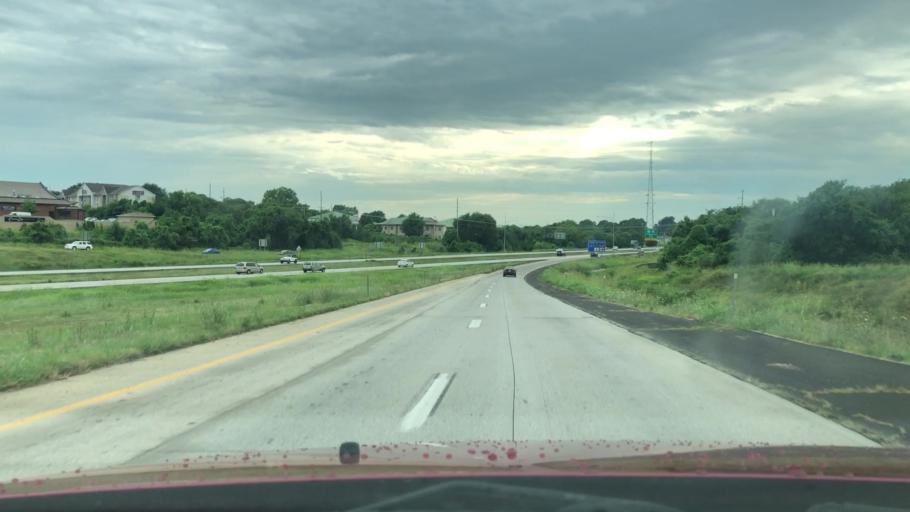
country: US
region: Missouri
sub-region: Greene County
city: Springfield
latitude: 37.1422
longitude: -93.2800
